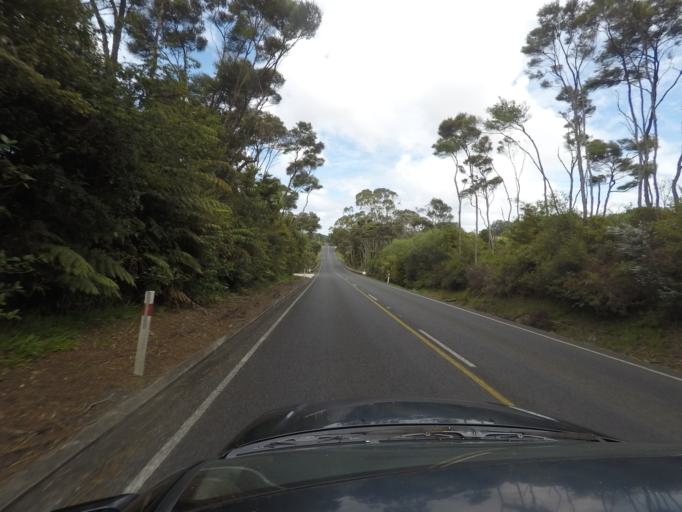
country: NZ
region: Auckland
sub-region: Auckland
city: Parakai
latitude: -36.6407
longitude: 174.5093
